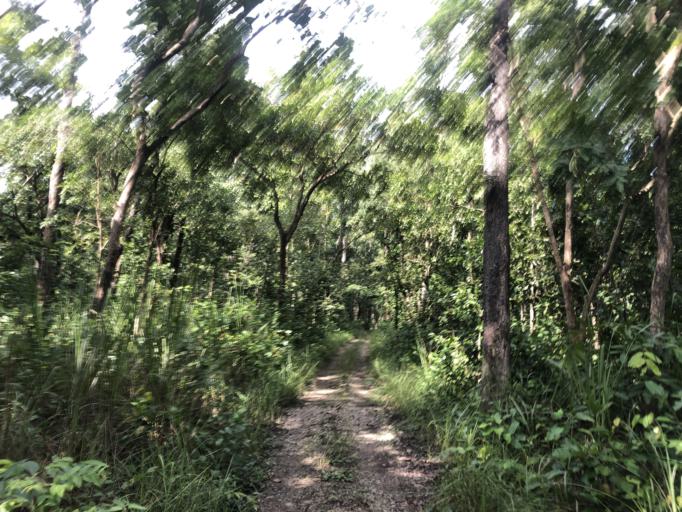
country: NP
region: Far Western
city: Tikapur
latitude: 28.5468
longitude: 81.2867
